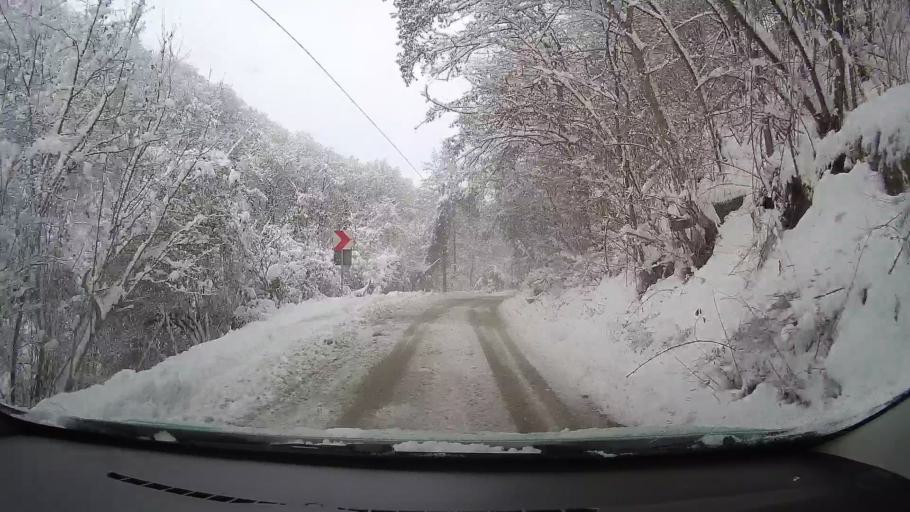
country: RO
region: Alba
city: Pianu de Sus
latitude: 45.8684
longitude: 23.4959
